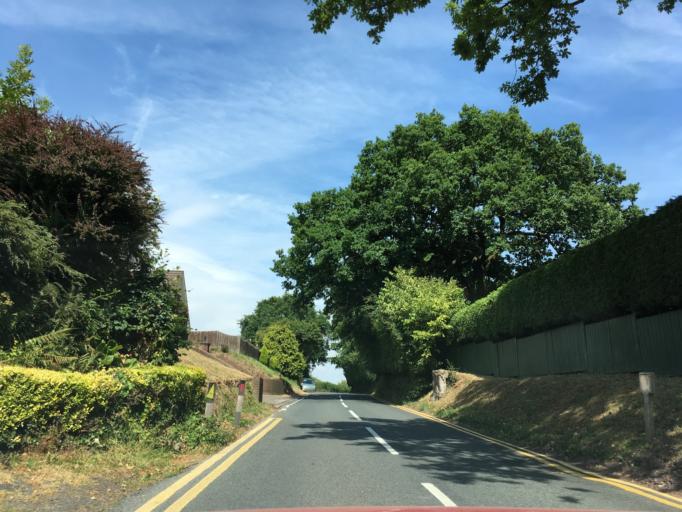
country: GB
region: Wales
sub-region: Newport
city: Caerleon
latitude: 51.5991
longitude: -2.9433
